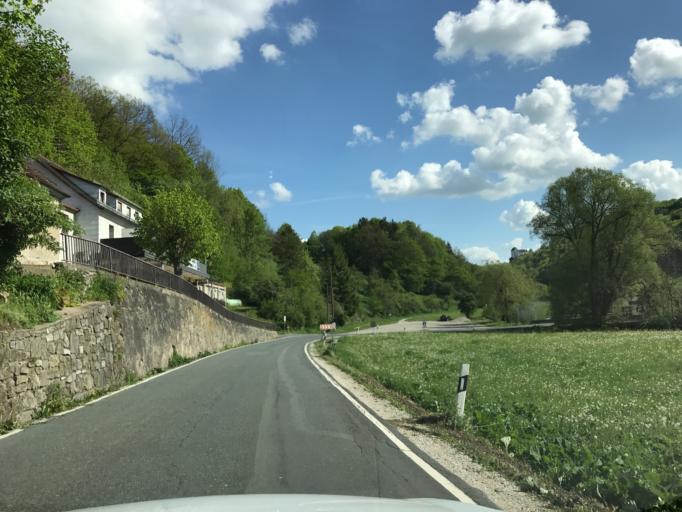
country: DE
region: Bavaria
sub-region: Upper Franconia
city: Egloffstein
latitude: 49.7131
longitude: 11.2565
